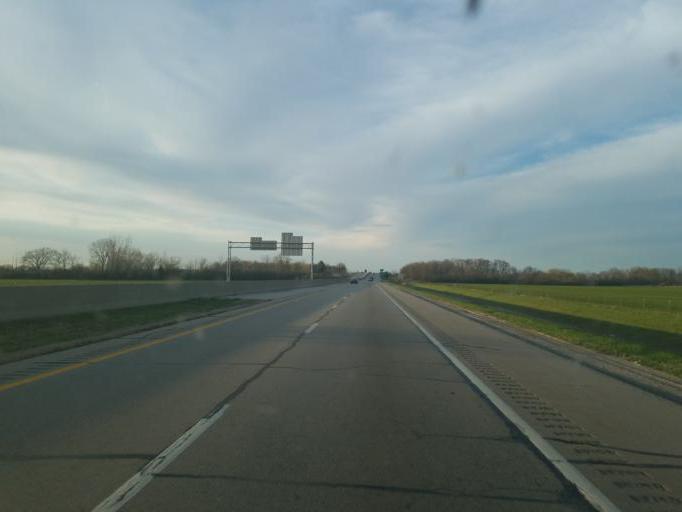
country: US
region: Ohio
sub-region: Wood County
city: Millbury
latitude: 41.5465
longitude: -83.4618
